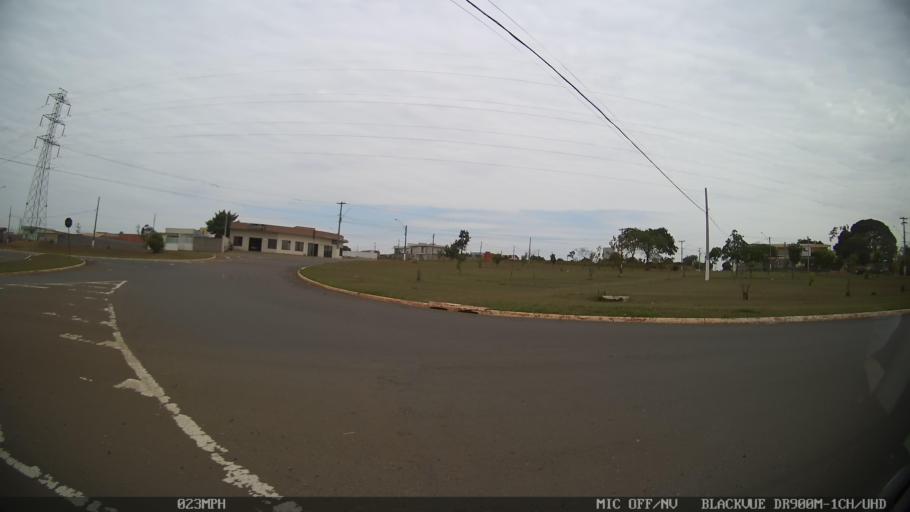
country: BR
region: Sao Paulo
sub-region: Paulinia
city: Paulinia
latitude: -22.7327
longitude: -47.1878
